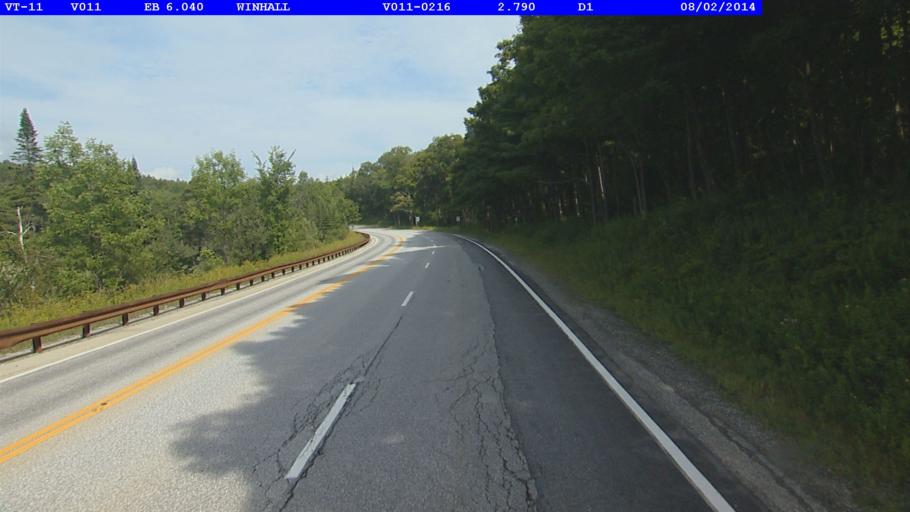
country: US
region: Vermont
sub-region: Bennington County
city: Manchester Center
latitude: 43.2060
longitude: -72.9672
